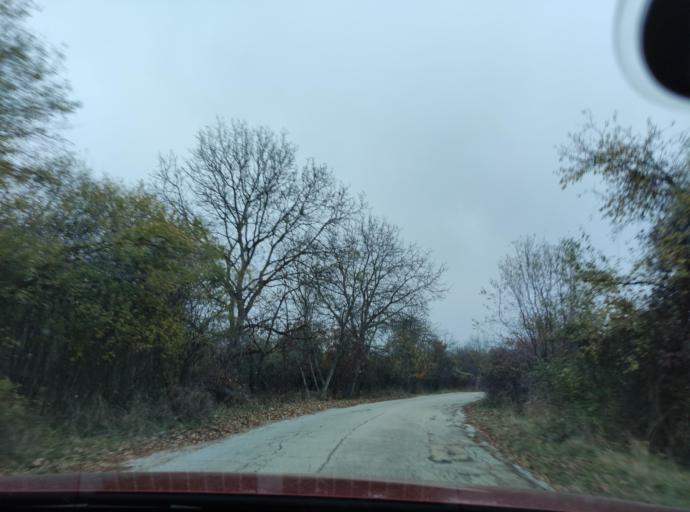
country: BG
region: Lovech
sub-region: Obshtina Yablanitsa
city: Yablanitsa
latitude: 43.0985
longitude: 24.0732
